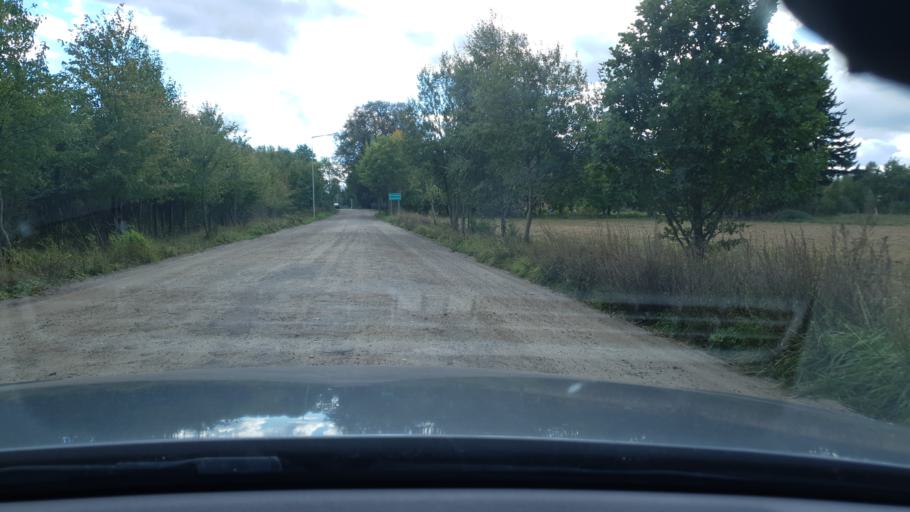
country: PL
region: Pomeranian Voivodeship
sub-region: Powiat wejherowski
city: Reda
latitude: 54.5812
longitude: 18.3128
